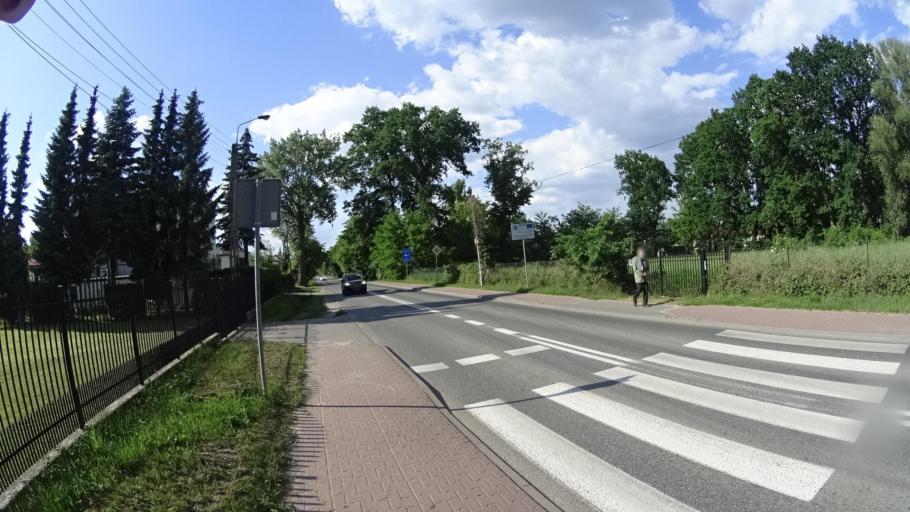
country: PL
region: Masovian Voivodeship
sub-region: Powiat pruszkowski
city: Nadarzyn
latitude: 52.0949
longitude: 20.8077
